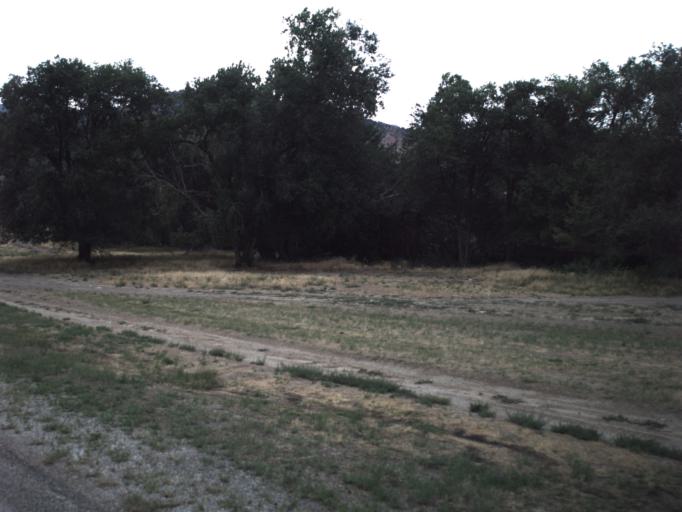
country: US
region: Utah
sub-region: Carbon County
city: East Carbon City
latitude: 39.5496
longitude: -110.3932
